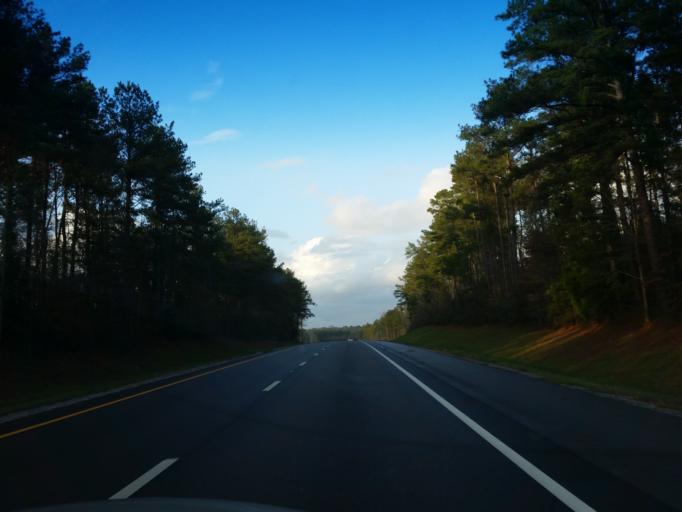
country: US
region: Mississippi
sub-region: Jones County
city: Sharon
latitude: 31.8591
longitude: -89.0470
